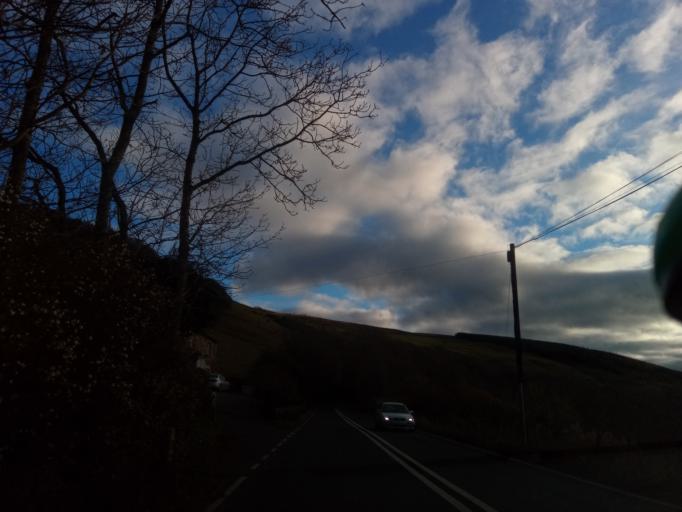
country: GB
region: Scotland
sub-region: The Scottish Borders
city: Galashiels
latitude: 55.6781
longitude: -2.8660
